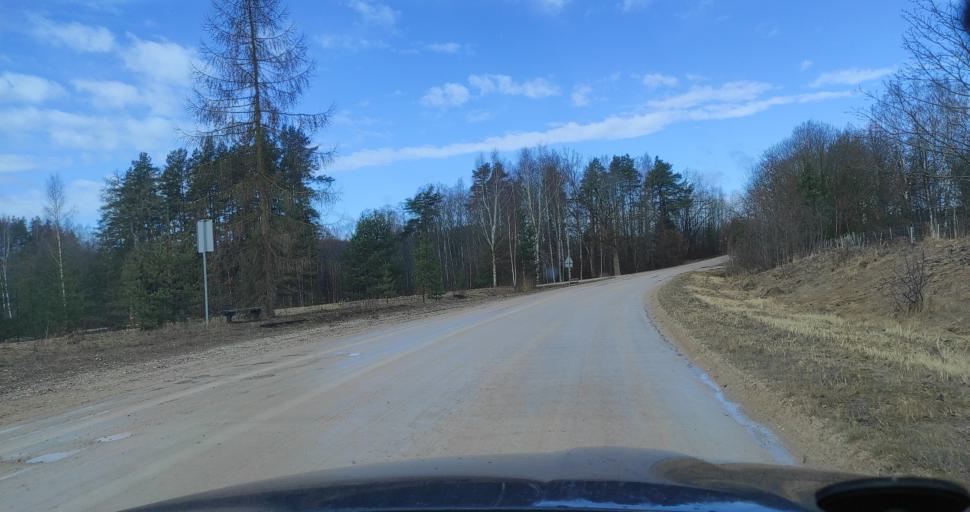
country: LV
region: Tukuma Rajons
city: Tukums
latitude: 57.1094
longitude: 23.0304
